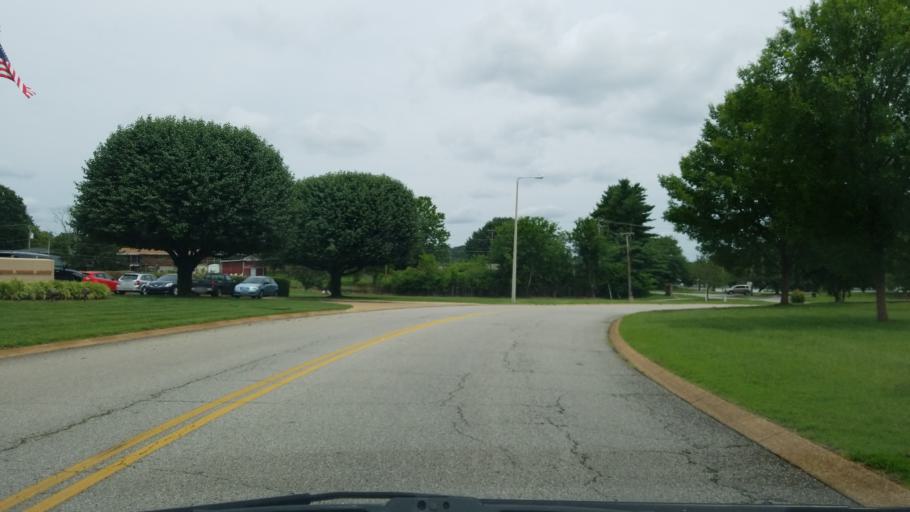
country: US
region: Tennessee
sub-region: Hamilton County
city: Harrison
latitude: 35.0750
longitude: -85.1836
